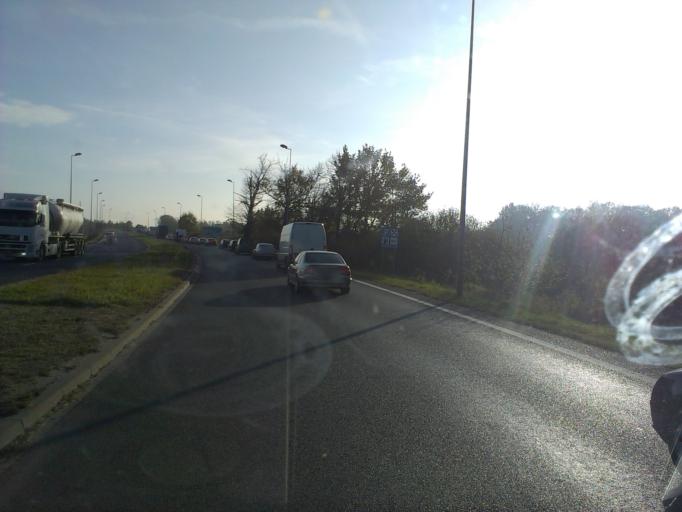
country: PL
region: Lower Silesian Voivodeship
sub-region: Legnica
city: Legnica
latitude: 51.1664
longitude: 16.1726
